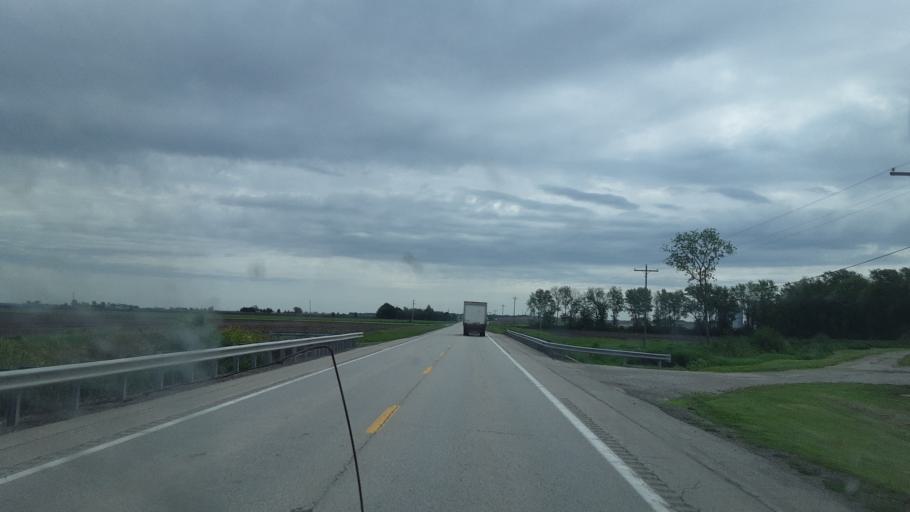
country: US
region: Illinois
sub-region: Mason County
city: Mason City
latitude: 40.3050
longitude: -89.6631
